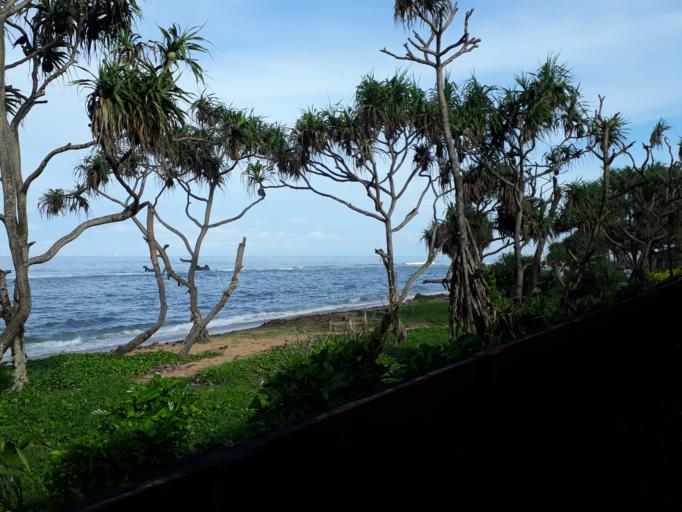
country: LK
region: Western
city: Galkissa
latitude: 6.8753
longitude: 79.8574
